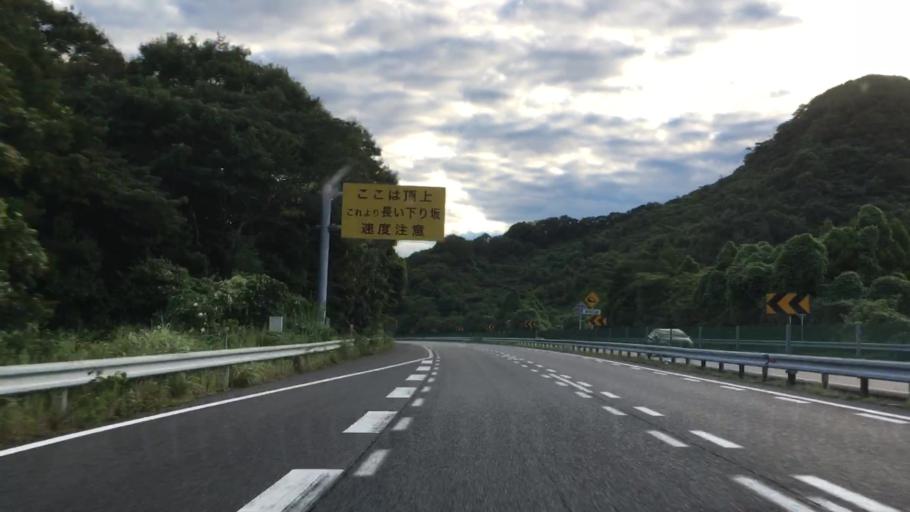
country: JP
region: Yamaguchi
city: Shimonoseki
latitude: 34.0399
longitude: 130.9723
